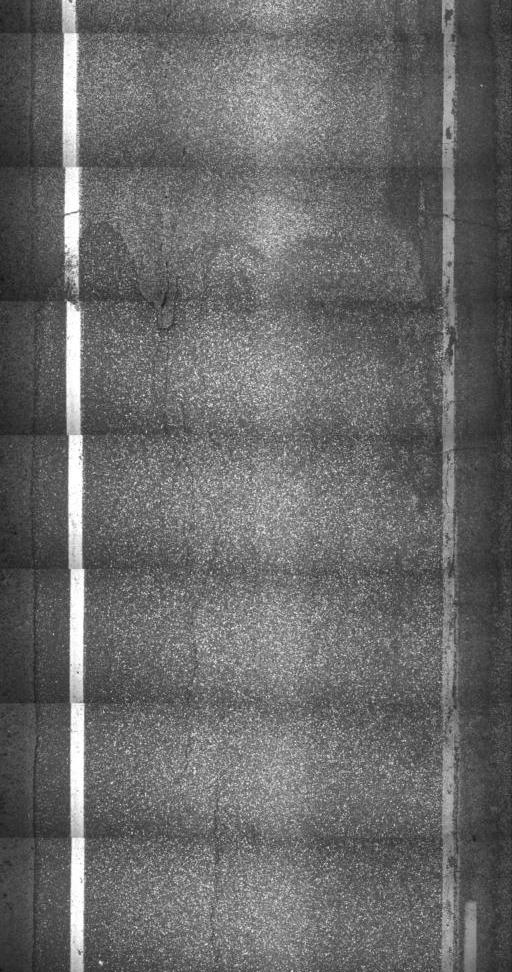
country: US
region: Vermont
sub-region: Washington County
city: Northfield
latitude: 44.1058
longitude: -72.7292
